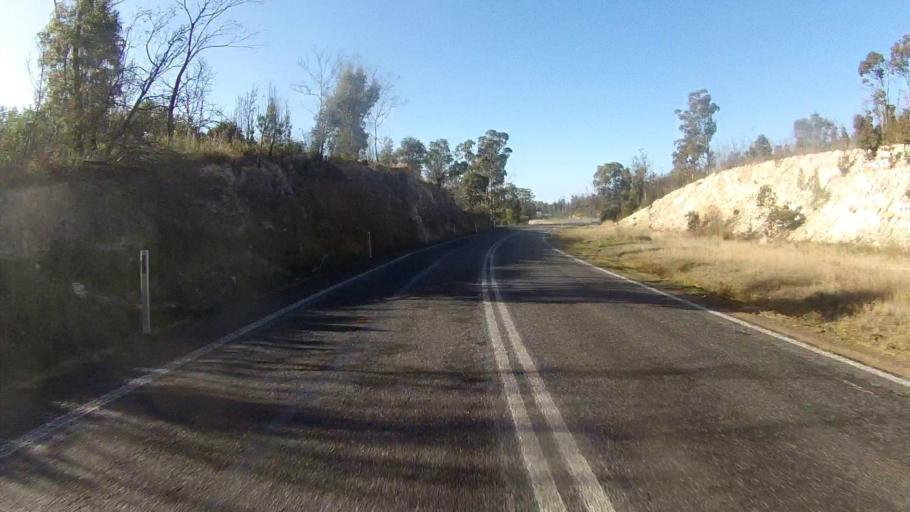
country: AU
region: Tasmania
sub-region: Sorell
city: Sorell
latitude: -42.8219
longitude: 147.6895
